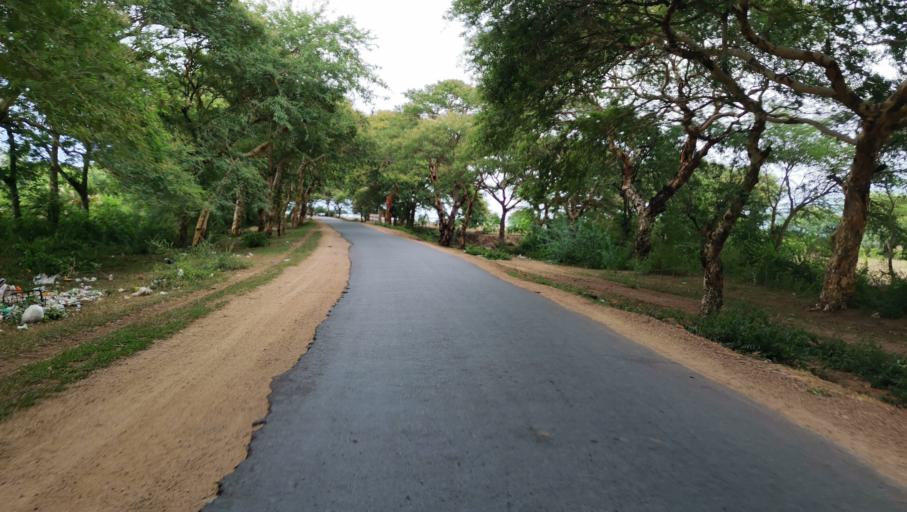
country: MM
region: Sagain
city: Monywa
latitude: 21.8549
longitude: 95.4387
